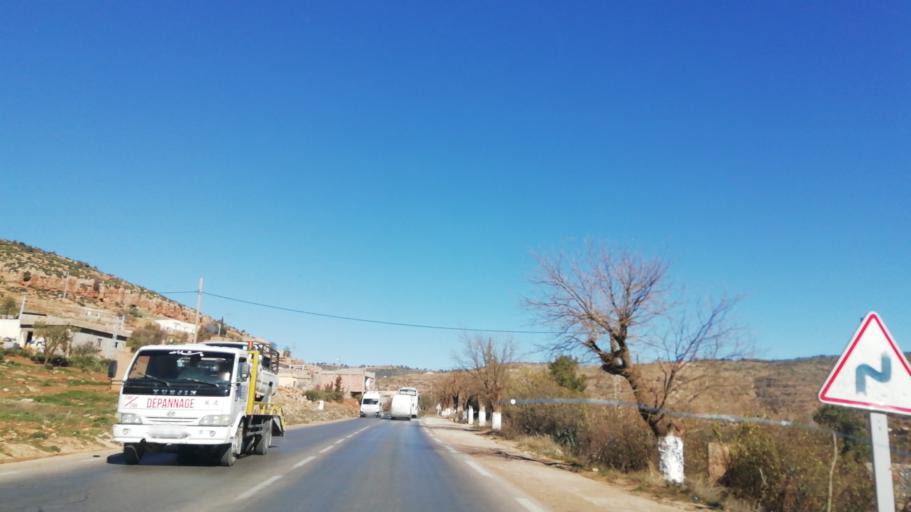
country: DZ
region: Tlemcen
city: Sebdou
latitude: 34.6918
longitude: -1.3140
